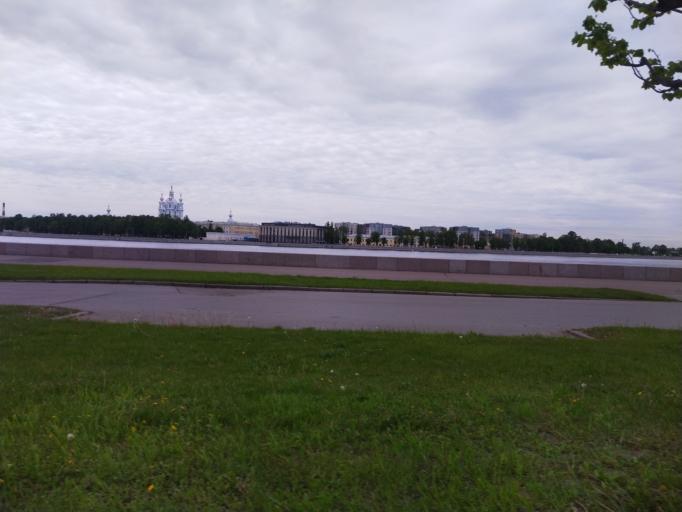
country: RU
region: Leningrad
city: Finlyandskiy
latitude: 59.9553
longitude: 30.4065
